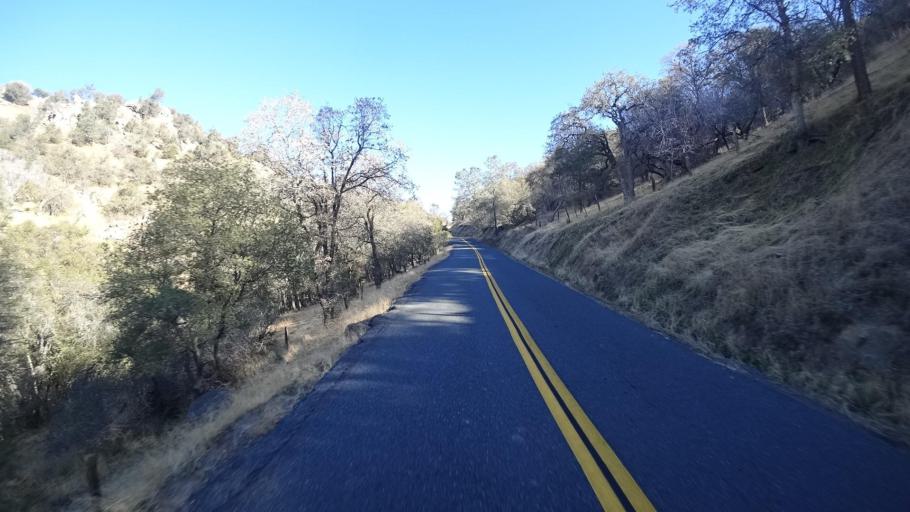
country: US
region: California
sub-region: Kern County
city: Alta Sierra
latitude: 35.7878
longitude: -118.7696
